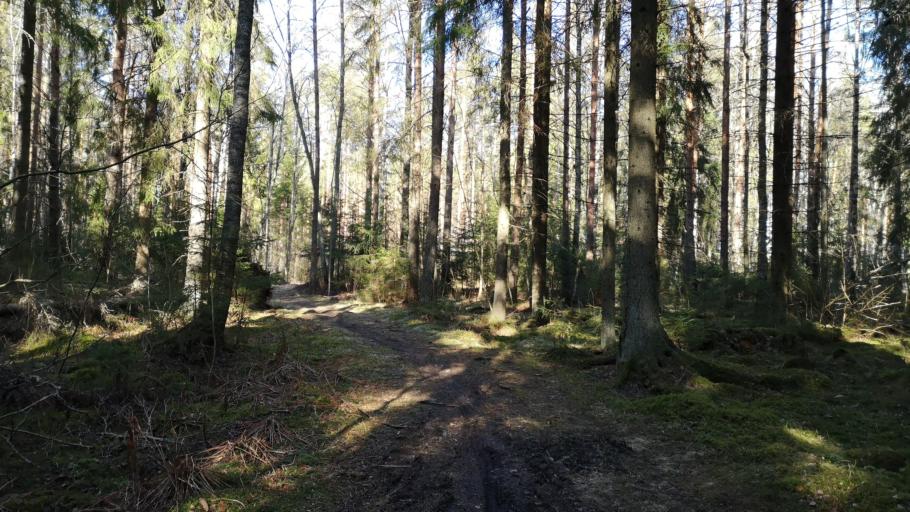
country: FI
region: Satakunta
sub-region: Pori
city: Pori
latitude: 61.4655
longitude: 21.7704
